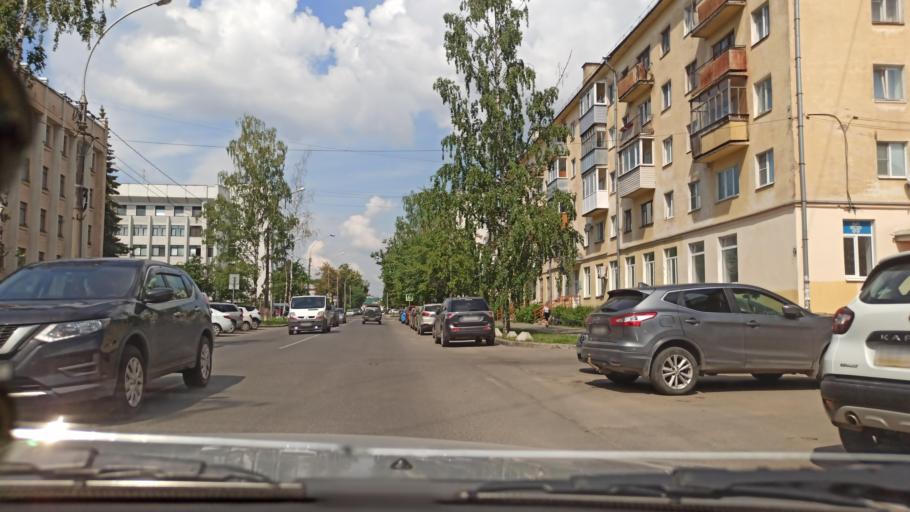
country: RU
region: Vologda
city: Vologda
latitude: 59.2165
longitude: 39.8914
